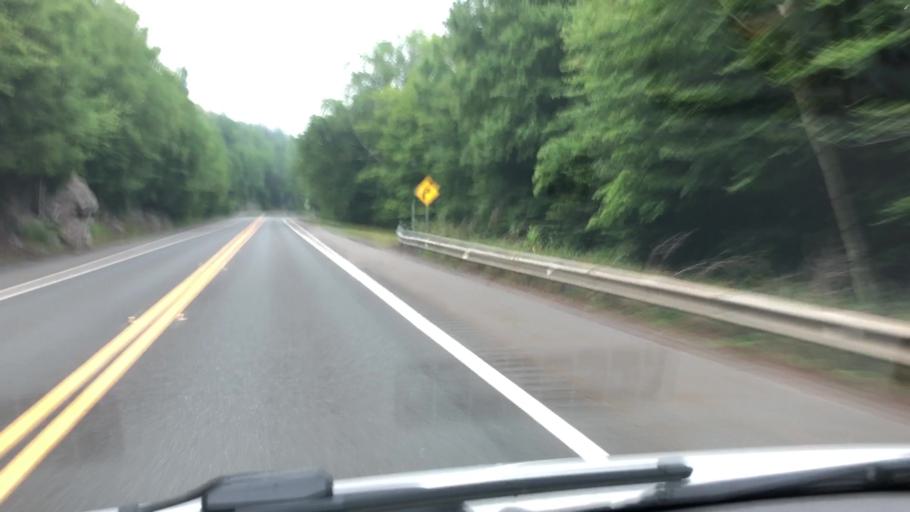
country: US
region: Massachusetts
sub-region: Hampshire County
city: Chesterfield
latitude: 42.4521
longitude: -72.8556
